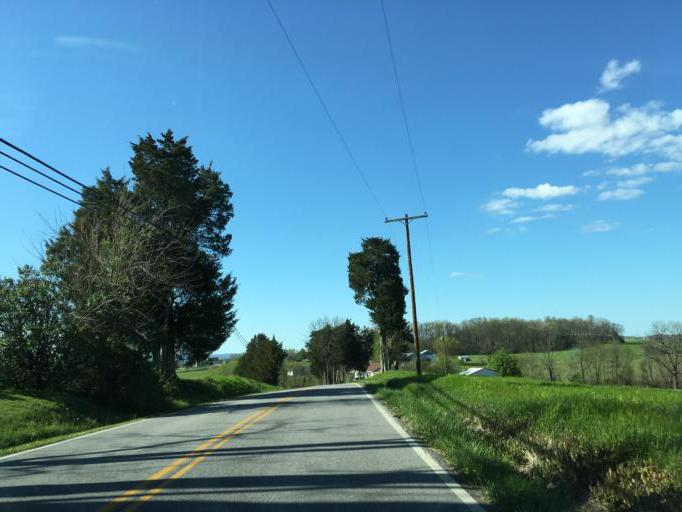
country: US
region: Maryland
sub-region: Frederick County
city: Emmitsburg
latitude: 39.6764
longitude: -77.3084
